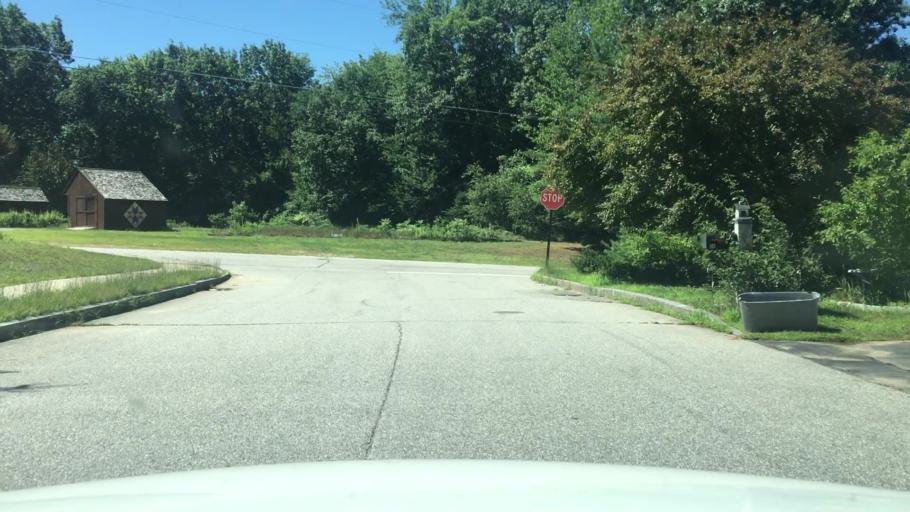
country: US
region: New Hampshire
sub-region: Merrimack County
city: Boscawen
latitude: 43.2700
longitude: -71.6003
